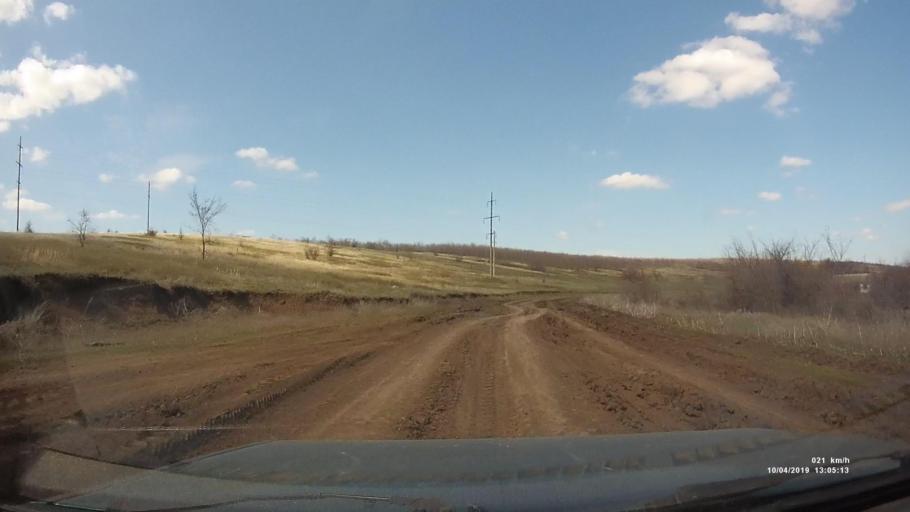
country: RU
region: Rostov
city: Masalovka
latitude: 48.3873
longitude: 40.2332
